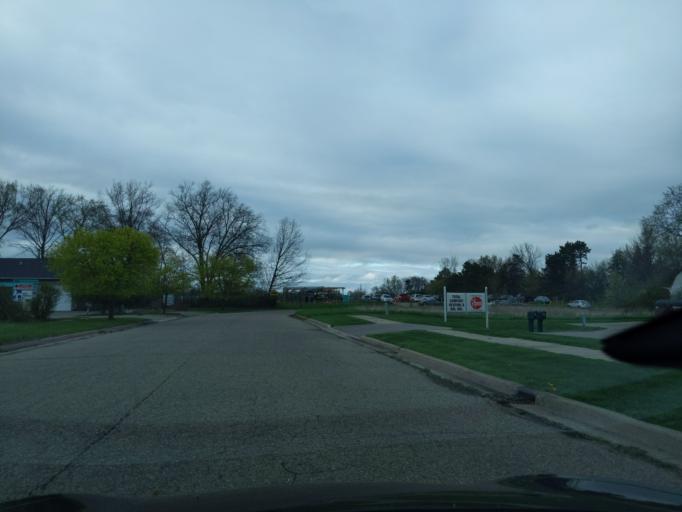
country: US
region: Michigan
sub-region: Ingham County
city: Edgemont Park
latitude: 42.7294
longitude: -84.5905
